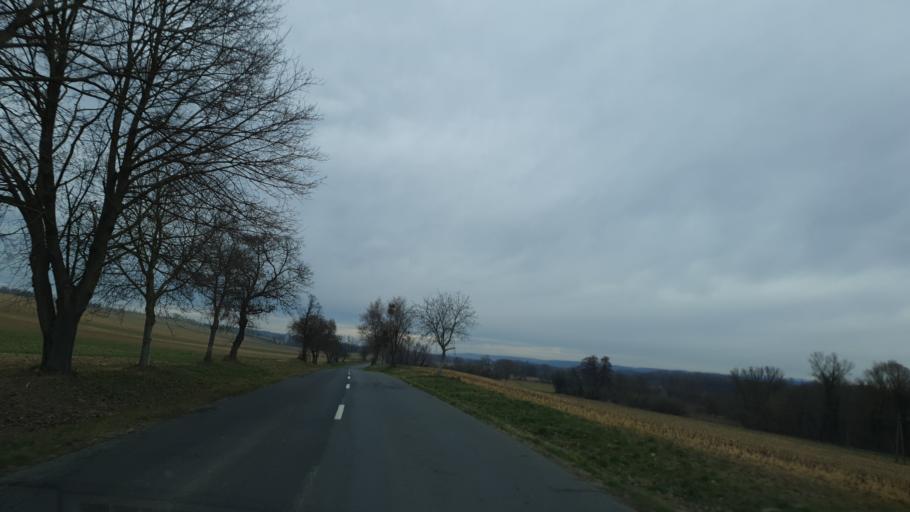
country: HU
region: Zala
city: Sarmellek
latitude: 46.6831
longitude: 17.1088
